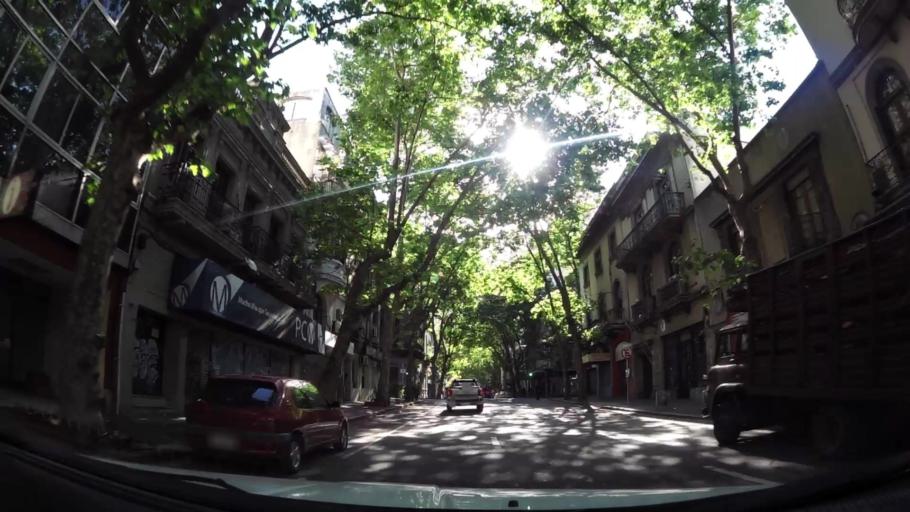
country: UY
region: Montevideo
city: Montevideo
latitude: -34.9070
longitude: -56.1931
